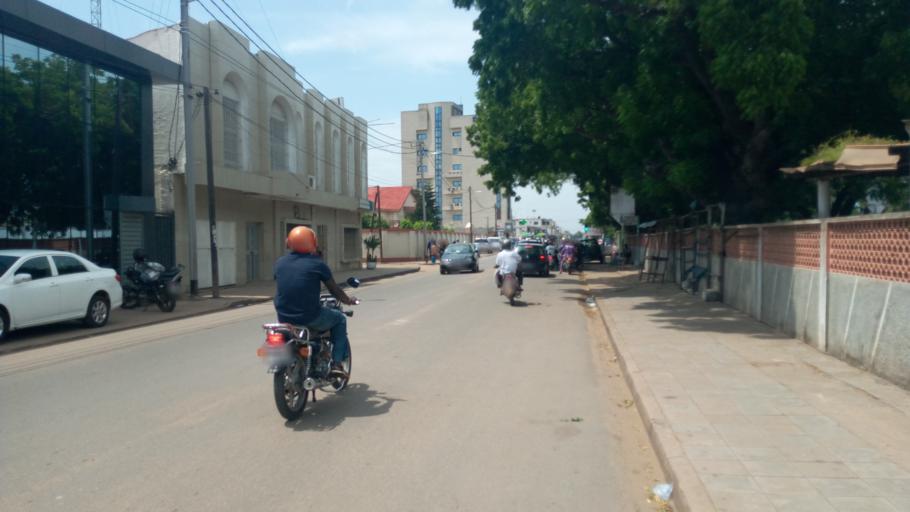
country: TG
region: Maritime
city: Lome
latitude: 6.1281
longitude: 1.2095
